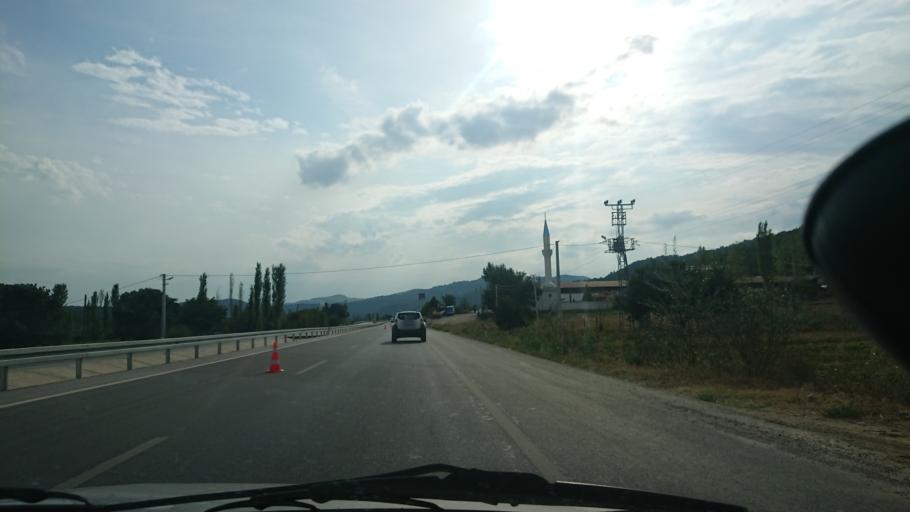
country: TR
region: Kuetahya
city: Gediz
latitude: 38.9386
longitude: 29.3184
